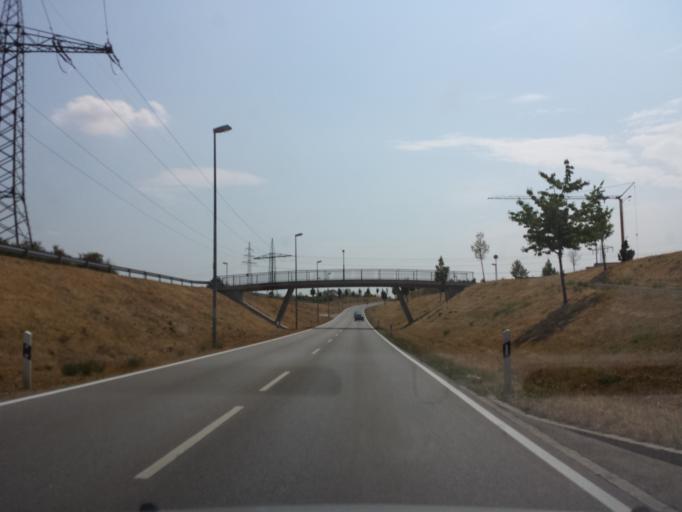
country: DE
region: Bavaria
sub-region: Swabia
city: Neu-Ulm
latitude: 48.4019
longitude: 10.0295
